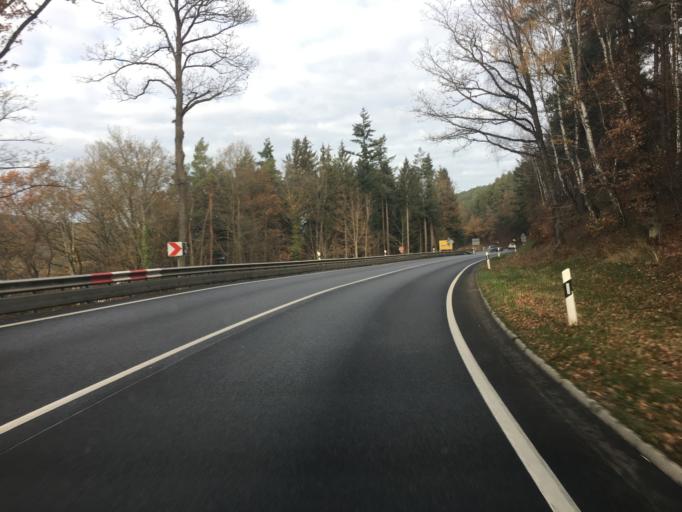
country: DE
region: North Rhine-Westphalia
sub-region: Regierungsbezirk Koln
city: Kall
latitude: 50.5551
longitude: 6.5423
